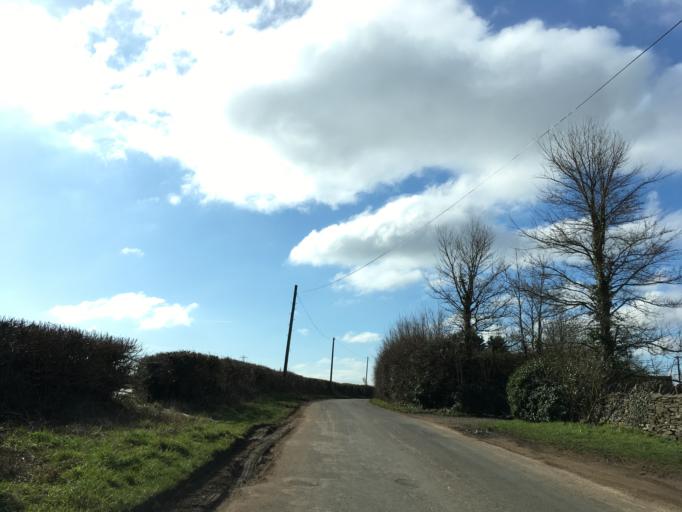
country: GB
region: England
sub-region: South Gloucestershire
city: Winterbourne
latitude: 51.5258
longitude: -2.5180
